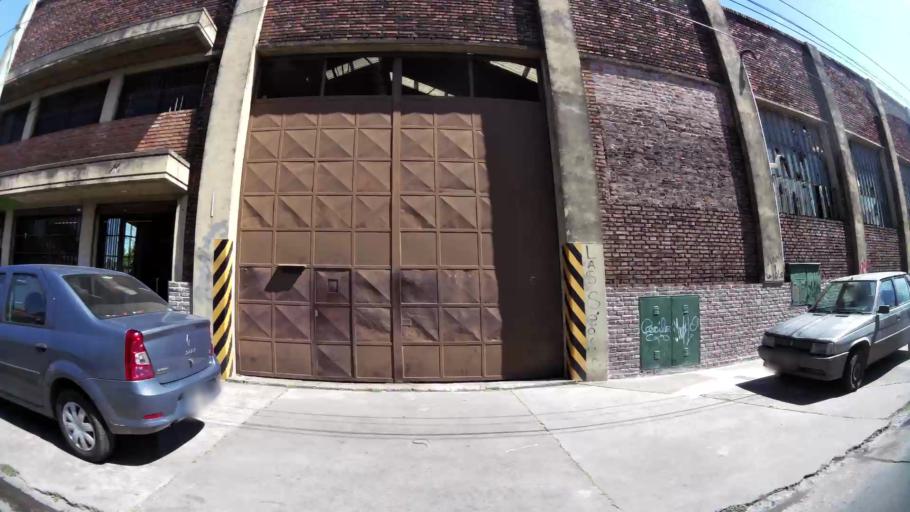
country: AR
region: Buenos Aires
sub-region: Partido de Quilmes
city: Quilmes
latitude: -34.7238
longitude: -58.3005
